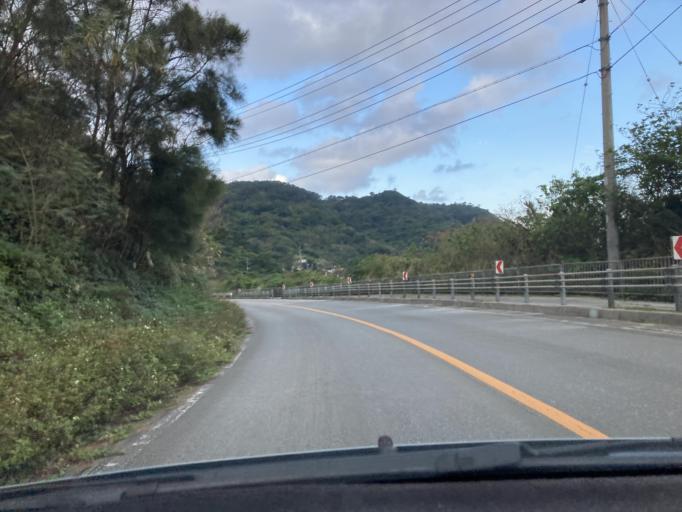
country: JP
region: Okinawa
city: Nago
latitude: 26.8340
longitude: 128.2873
